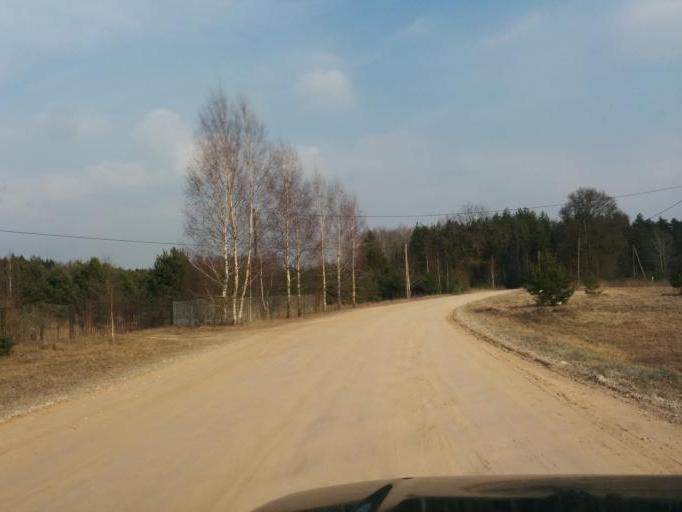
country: LV
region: Olaine
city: Olaine
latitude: 56.7909
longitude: 24.0005
